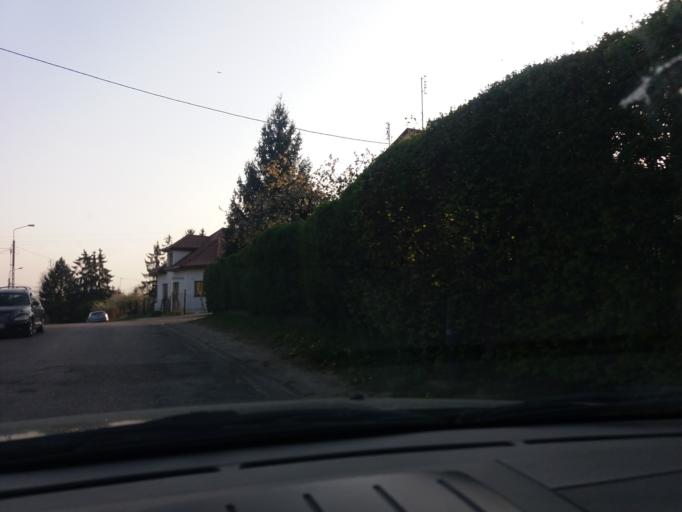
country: PL
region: Masovian Voivodeship
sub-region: Powiat mlawski
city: Mlawa
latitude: 53.1250
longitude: 20.3633
